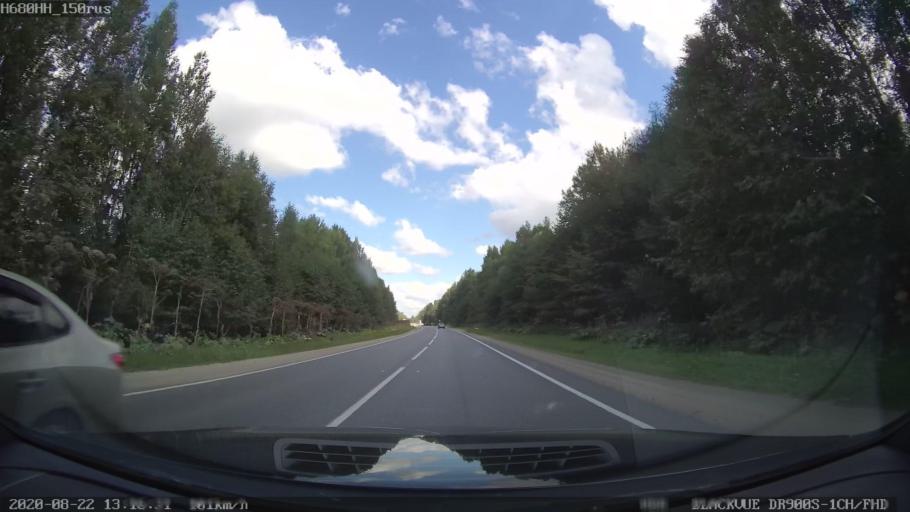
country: RU
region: Tverskaya
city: Bezhetsk
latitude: 57.7651
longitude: 36.6568
